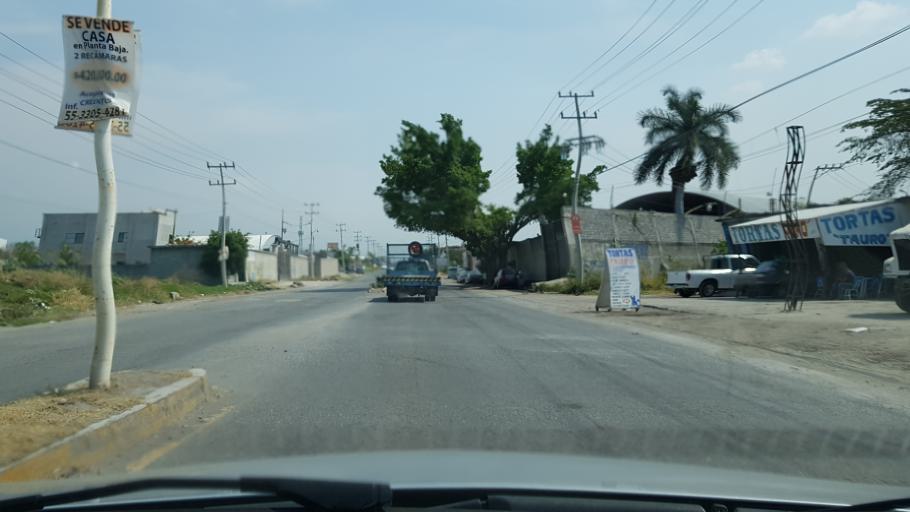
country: MX
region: Morelos
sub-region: Xochitepec
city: Chiconcuac
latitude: 18.7976
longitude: -99.1997
